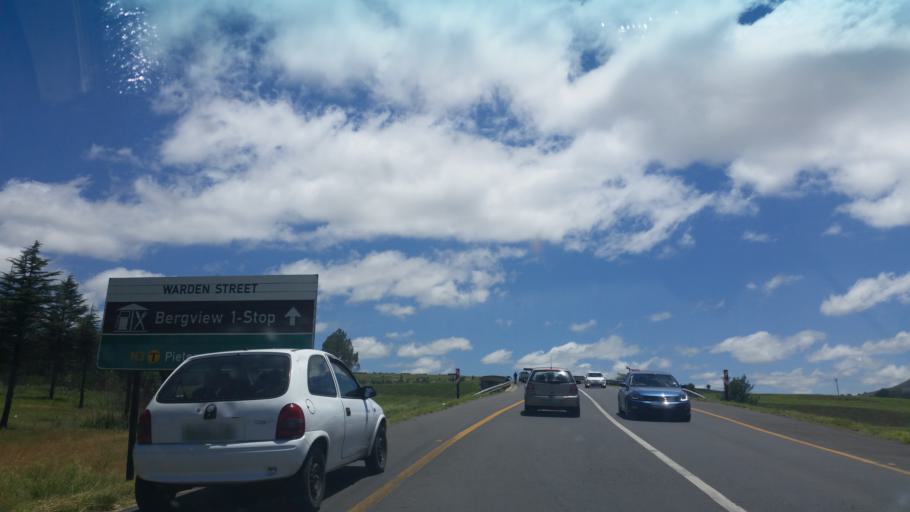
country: ZA
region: Orange Free State
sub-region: Thabo Mofutsanyana District Municipality
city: Harrismith
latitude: -28.2605
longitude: 29.1175
